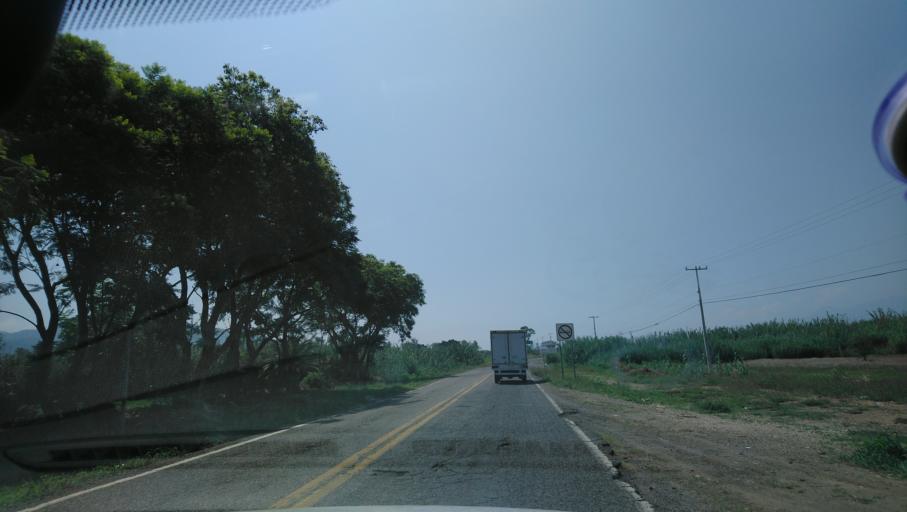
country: MX
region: Oaxaca
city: Santa Maria del Tule
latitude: 17.0398
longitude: -96.6220
